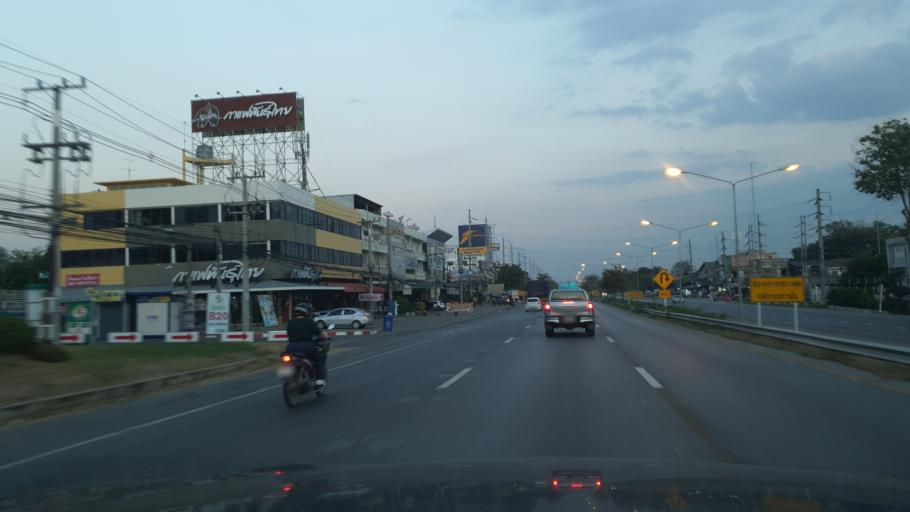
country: TH
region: Nakhon Sawan
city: Nakhon Sawan
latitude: 15.7071
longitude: 100.1008
